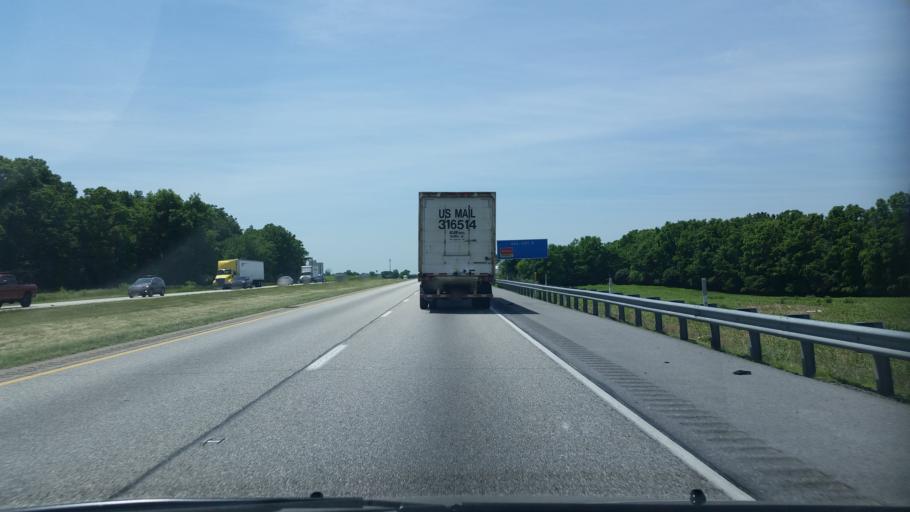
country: US
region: Pennsylvania
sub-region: Franklin County
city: Greencastle
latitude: 39.7674
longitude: -77.7216
